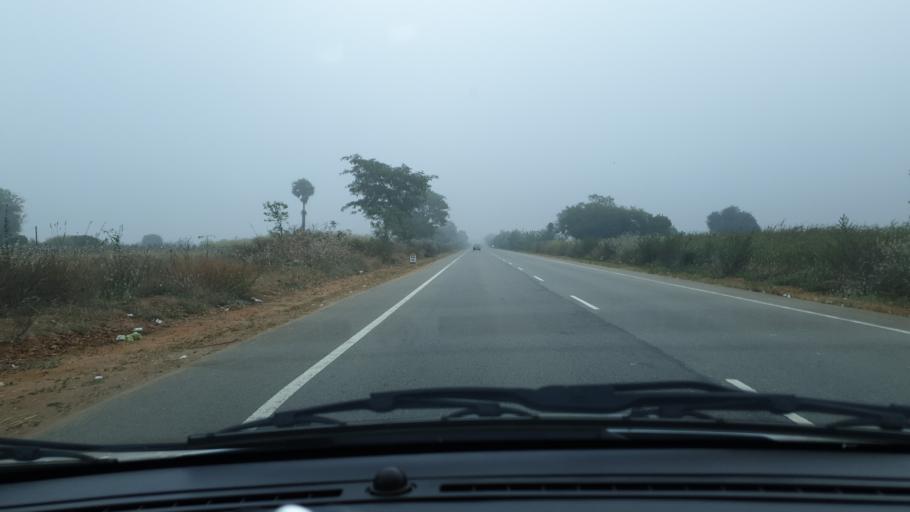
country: IN
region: Telangana
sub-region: Nalgonda
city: Devarkonda
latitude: 16.6354
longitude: 78.6375
